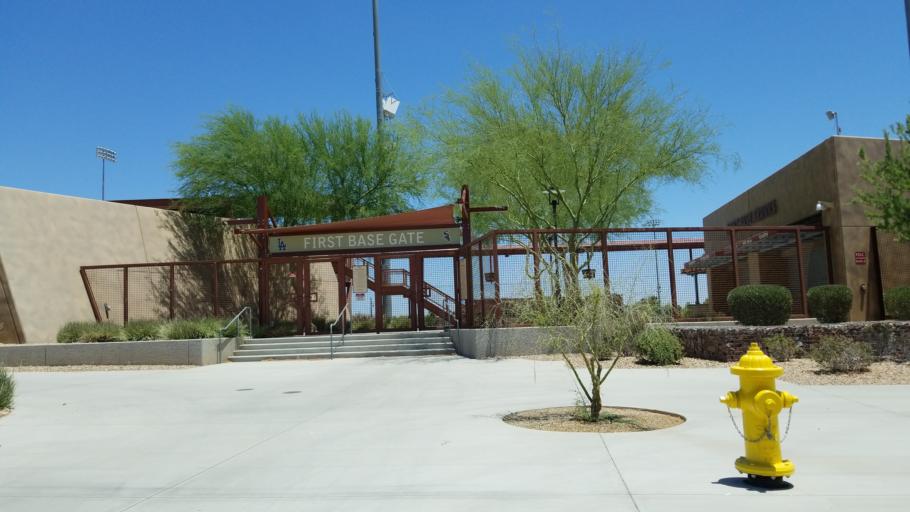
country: US
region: Arizona
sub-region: Maricopa County
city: Litchfield Park
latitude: 33.5146
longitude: -112.2971
